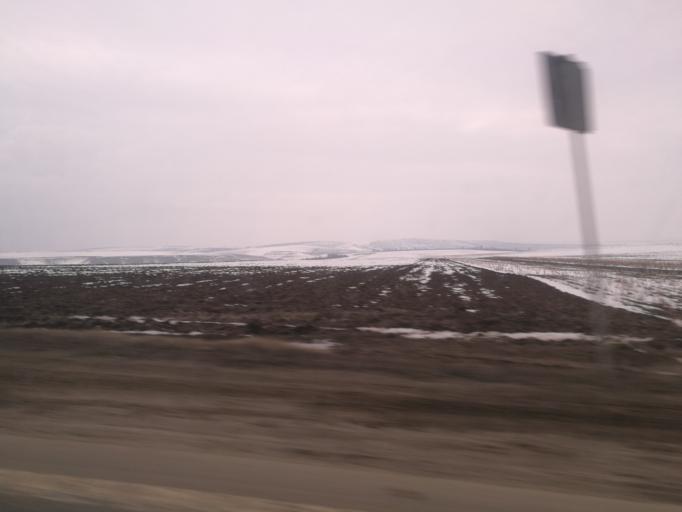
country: RO
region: Iasi
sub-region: Comuna Ruginoasa
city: Dumbravita
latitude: 47.2336
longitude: 26.8143
